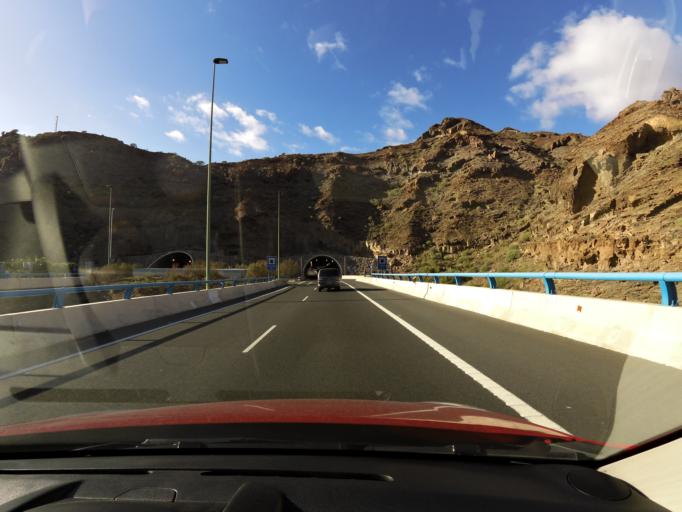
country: ES
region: Canary Islands
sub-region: Provincia de Las Palmas
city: Puerto Rico
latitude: 27.7981
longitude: -15.7022
